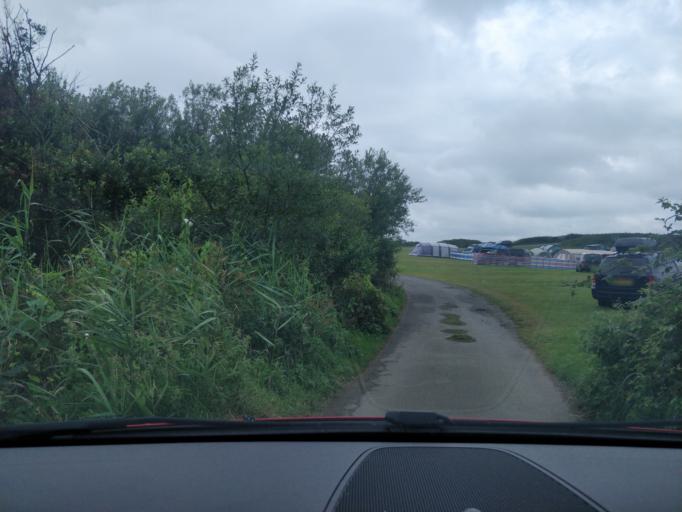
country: GB
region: Wales
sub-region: Gwynedd
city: Llanfair
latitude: 52.8206
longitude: -4.1397
